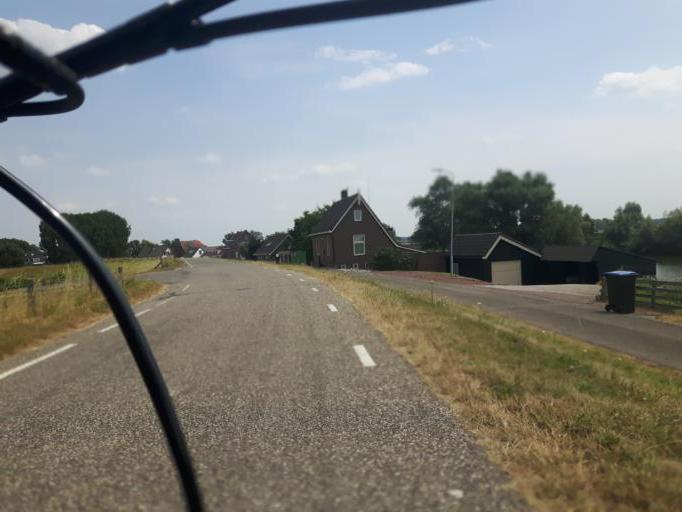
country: NL
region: Gelderland
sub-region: Gemeente Zaltbommel
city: Nederhemert
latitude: 51.8190
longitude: 5.1435
